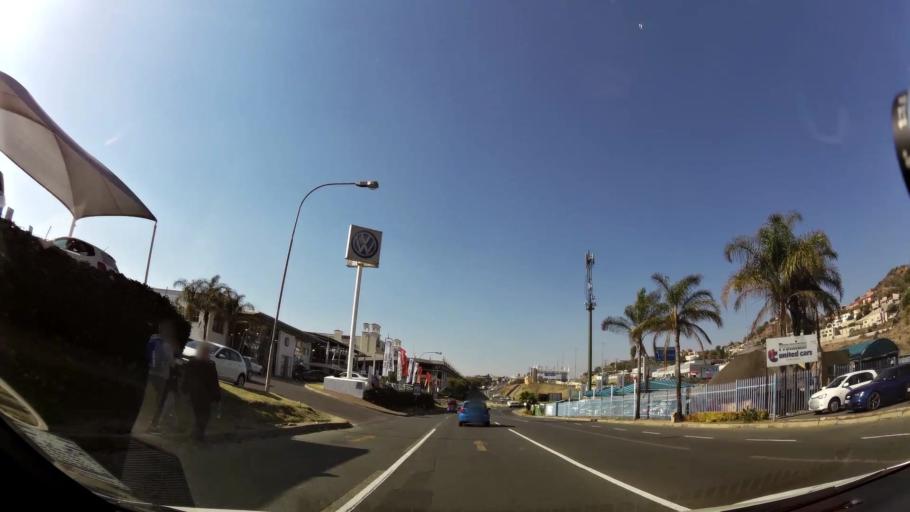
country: ZA
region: Gauteng
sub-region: City of Johannesburg Metropolitan Municipality
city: Johannesburg
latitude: -26.2699
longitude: 28.0467
